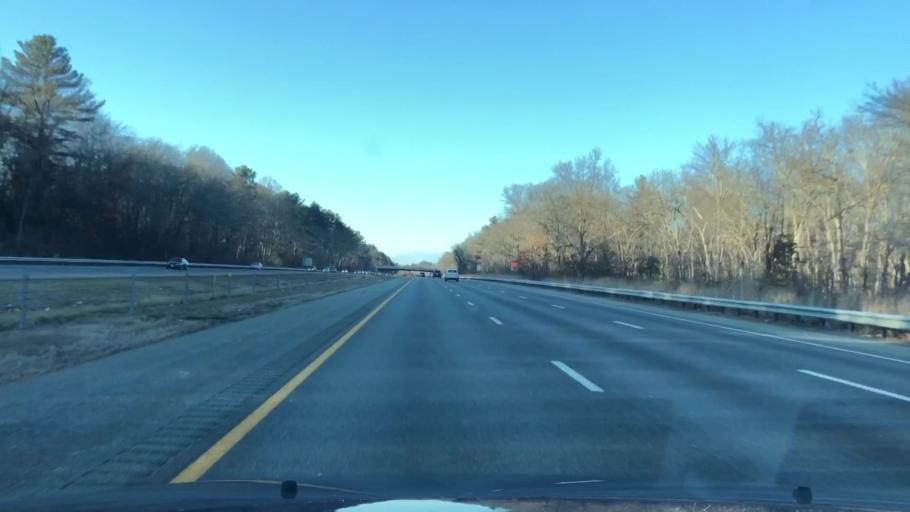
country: US
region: Massachusetts
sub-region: Middlesex County
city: Pinehurst
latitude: 42.5116
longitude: -71.2526
